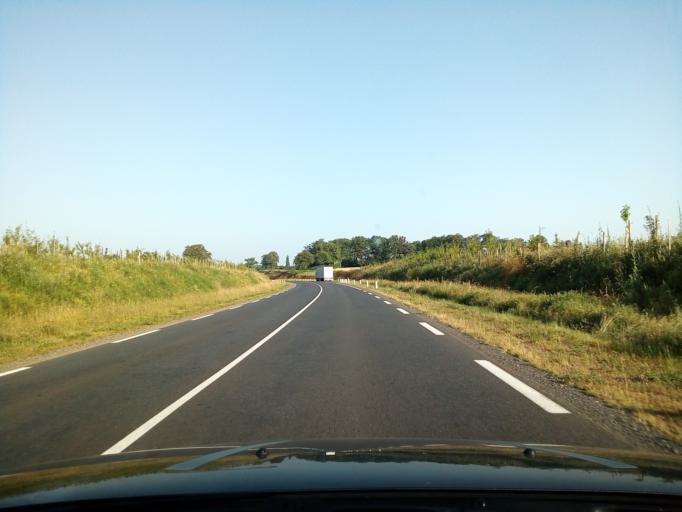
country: FR
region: Limousin
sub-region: Departement de la Haute-Vienne
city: Bussiere-Poitevine
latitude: 46.1158
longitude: 0.9178
